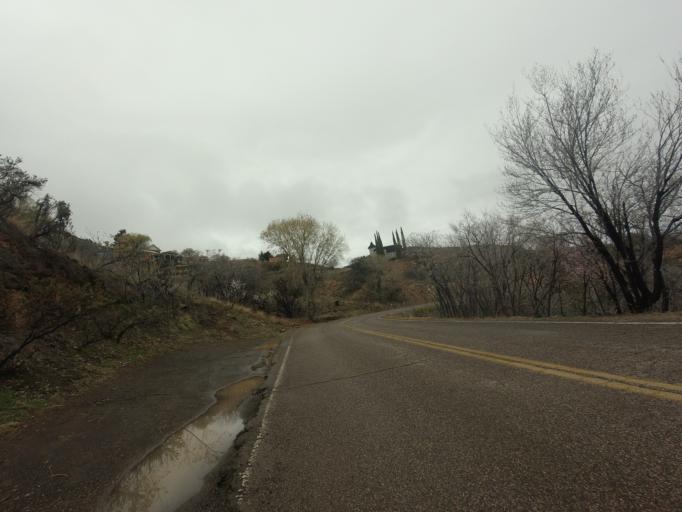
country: US
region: Arizona
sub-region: Yavapai County
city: Clarkdale
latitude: 34.7499
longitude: -112.1119
